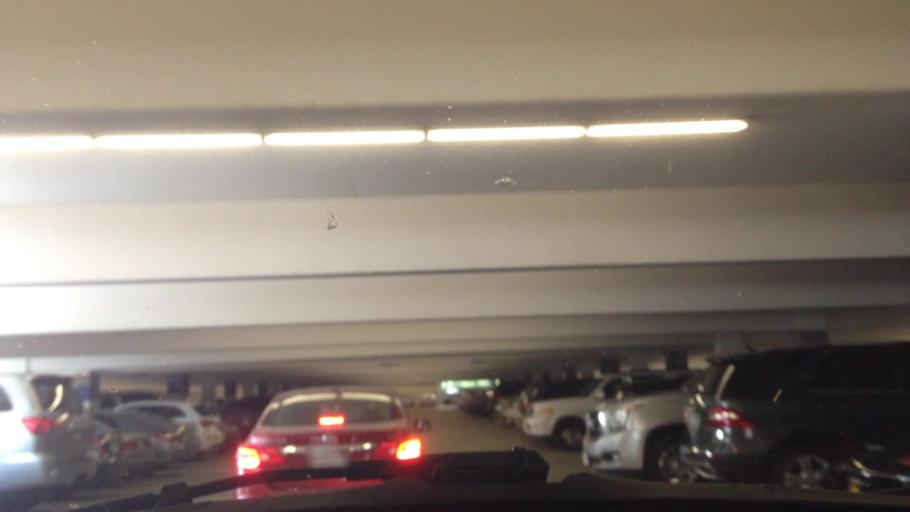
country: US
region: California
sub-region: Orange County
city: Costa Mesa
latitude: 33.6888
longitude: -117.8949
